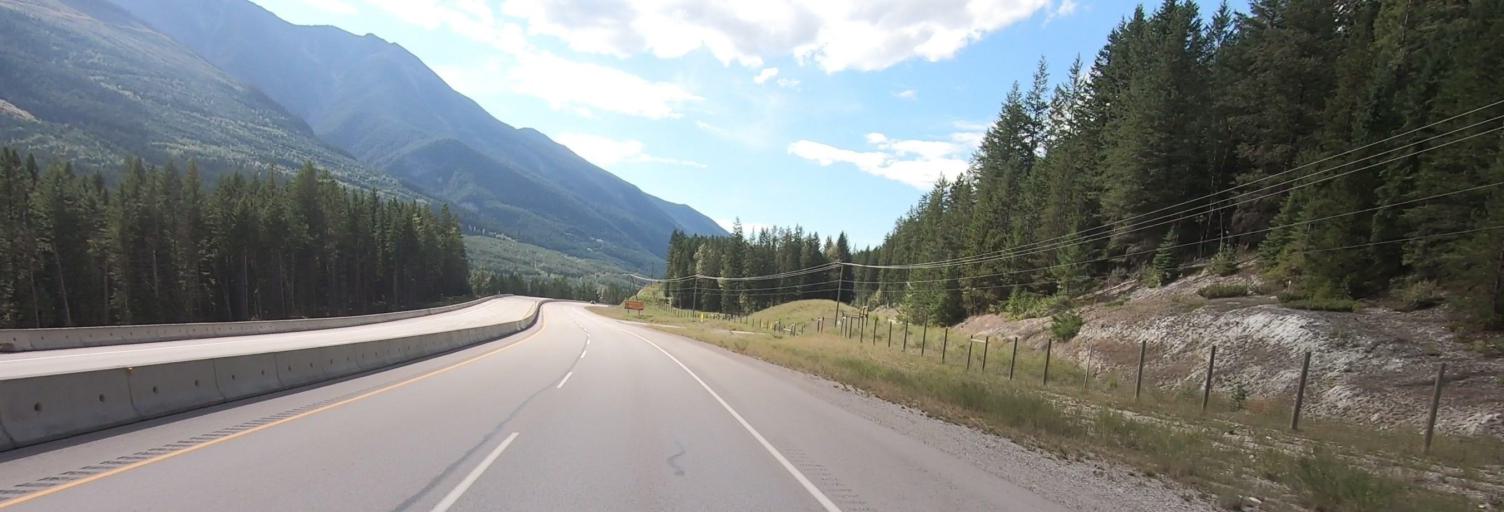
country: CA
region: British Columbia
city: Golden
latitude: 51.2605
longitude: -116.7221
